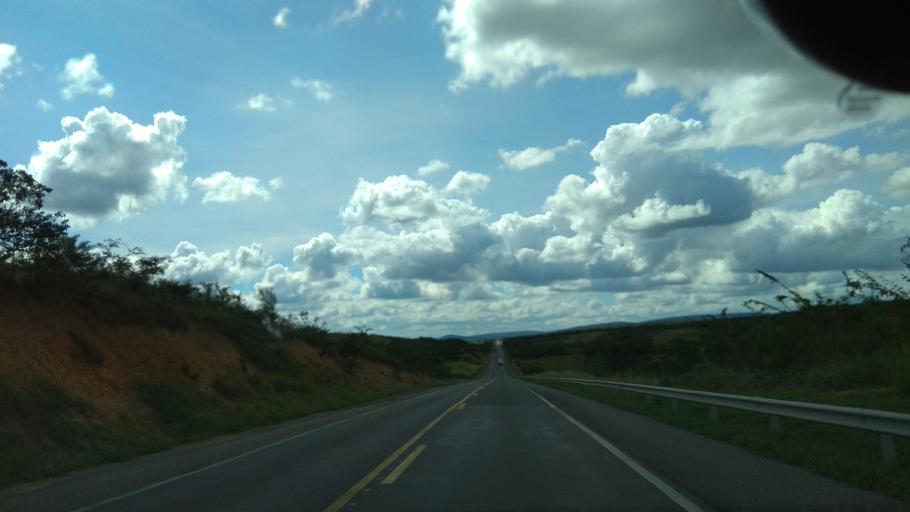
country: BR
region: Bahia
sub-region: Jaguaquara
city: Jaguaquara
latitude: -13.4528
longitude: -40.0319
